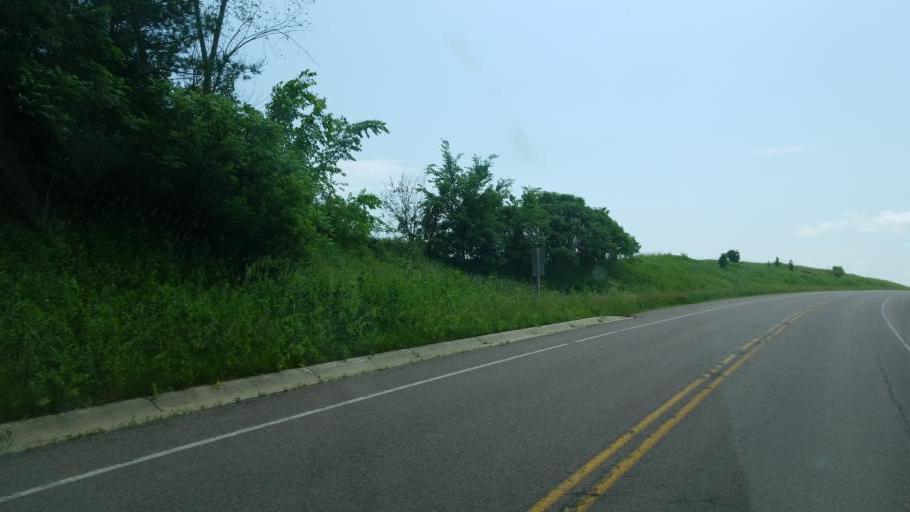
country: US
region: Wisconsin
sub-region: Monroe County
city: Cashton
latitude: 43.6495
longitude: -90.5958
